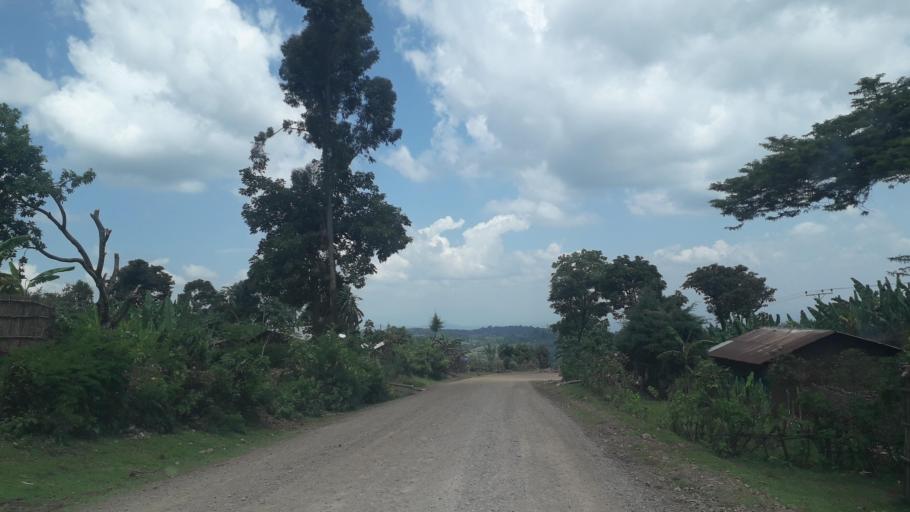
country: ET
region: Oromiya
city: Jima
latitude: 7.4658
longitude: 36.8747
